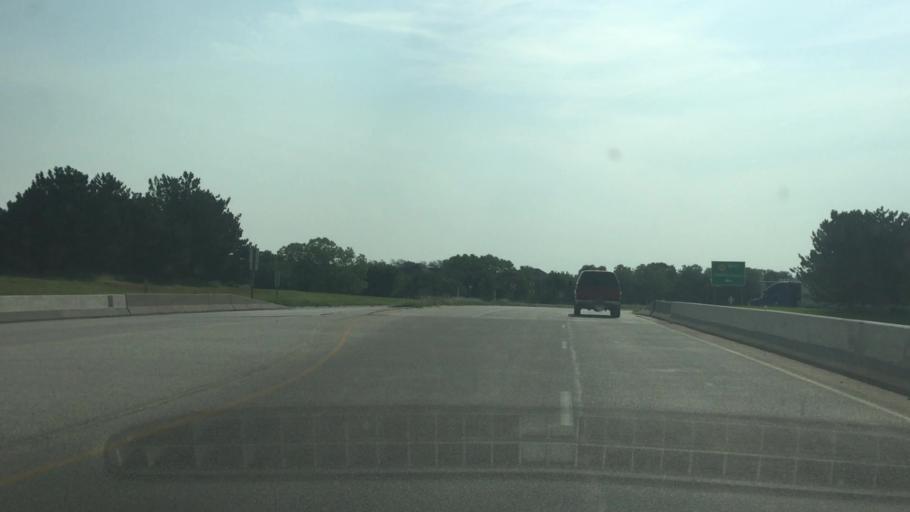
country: US
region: Kansas
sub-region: Butler County
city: Andover
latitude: 37.6902
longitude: -97.1857
